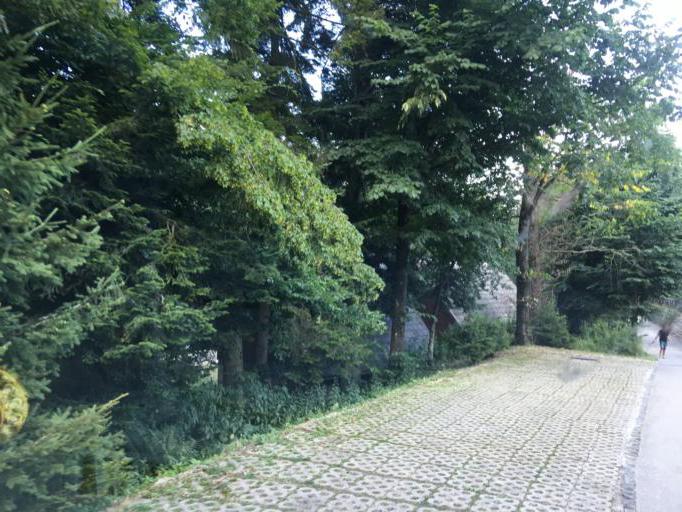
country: SI
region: Postojna
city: Postojna
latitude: 45.8053
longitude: 14.2042
